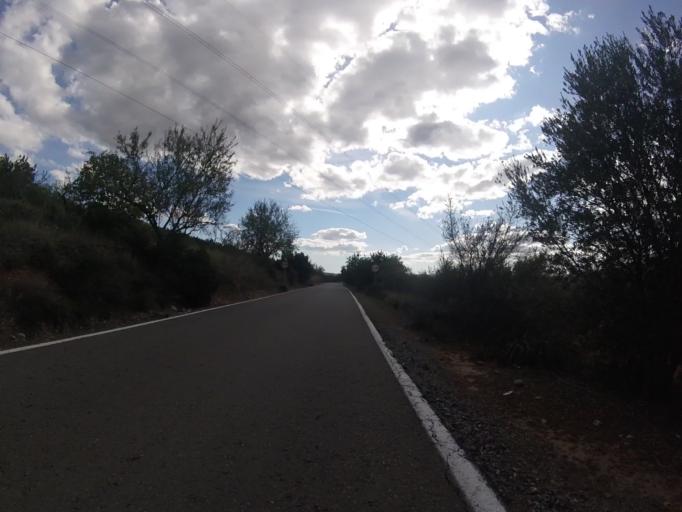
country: ES
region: Valencia
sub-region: Provincia de Castello
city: Cuevas de Vinroma
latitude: 40.3586
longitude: 0.1255
